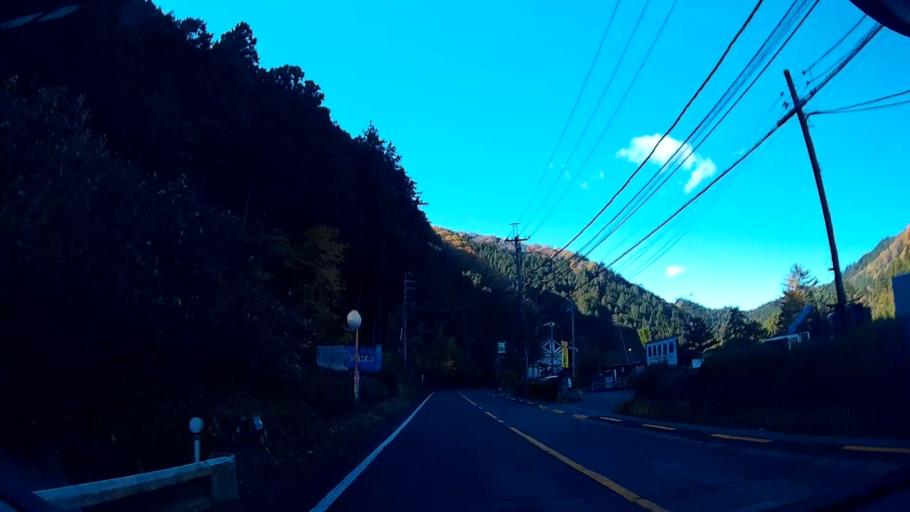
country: JP
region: Tokyo
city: Itsukaichi
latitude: 35.7233
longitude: 139.1770
